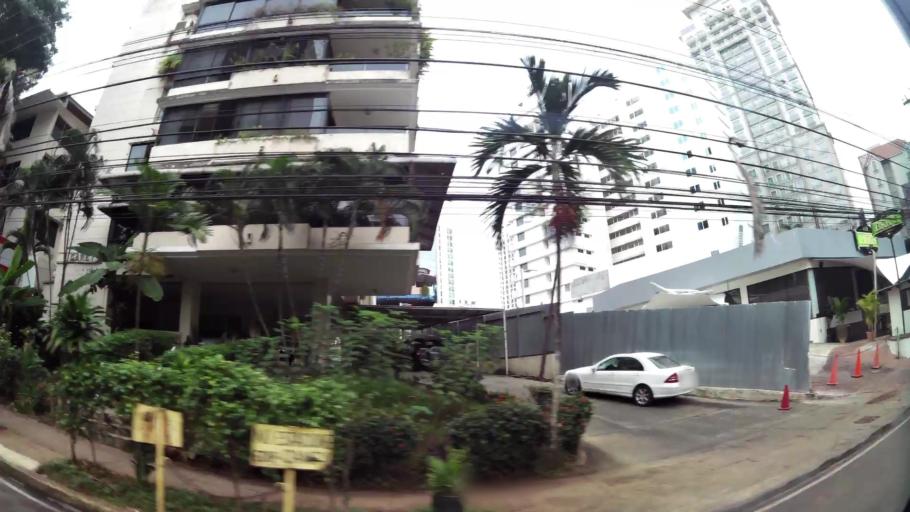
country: PA
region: Panama
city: Panama
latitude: 8.9802
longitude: -79.5258
